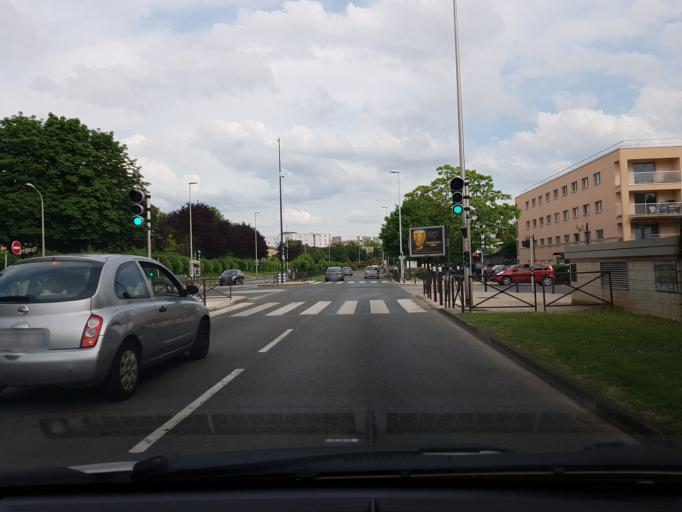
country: FR
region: Ile-de-France
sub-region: Departement de Seine-et-Marne
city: Torcy
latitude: 48.8444
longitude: 2.6490
